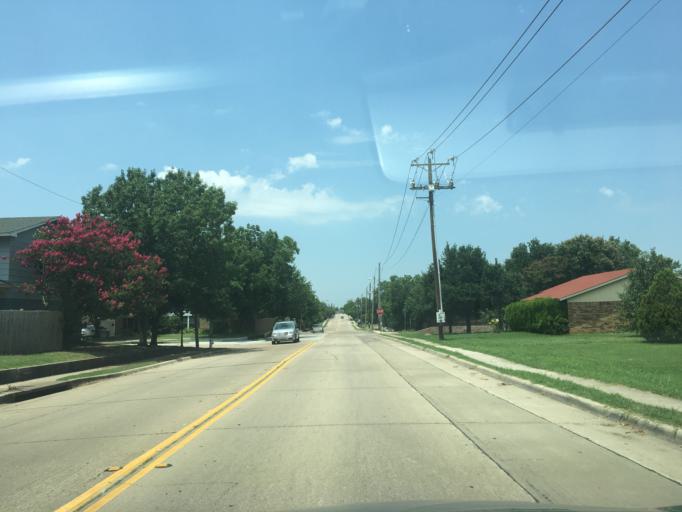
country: US
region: Texas
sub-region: Dallas County
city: Carrollton
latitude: 32.9463
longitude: -96.8796
